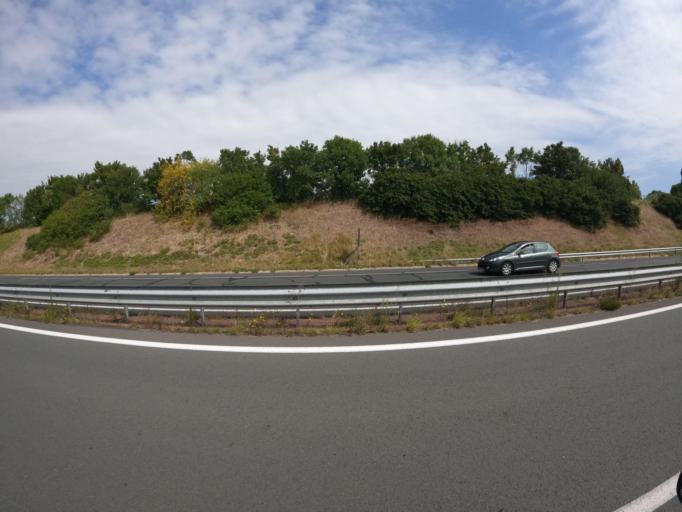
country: FR
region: Poitou-Charentes
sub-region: Departement de la Charente-Maritime
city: Saint-Jean-de-Liversay
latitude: 46.2246
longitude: -0.8610
